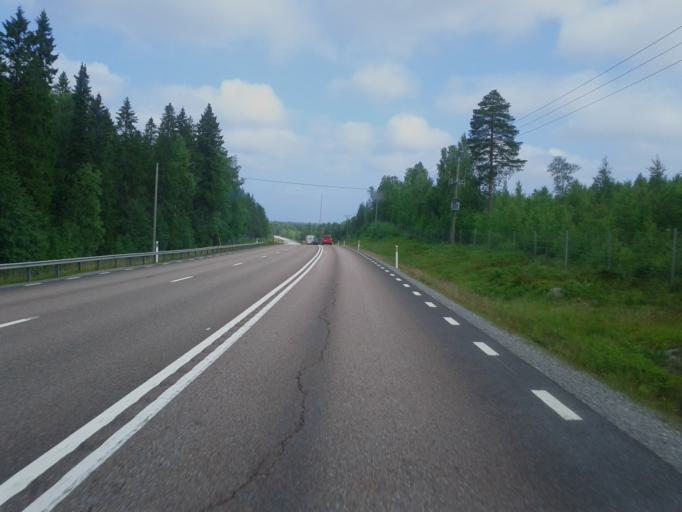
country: SE
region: Vaesterbotten
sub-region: Skelleftea Kommun
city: Burea
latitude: 64.4598
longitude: 21.2906
